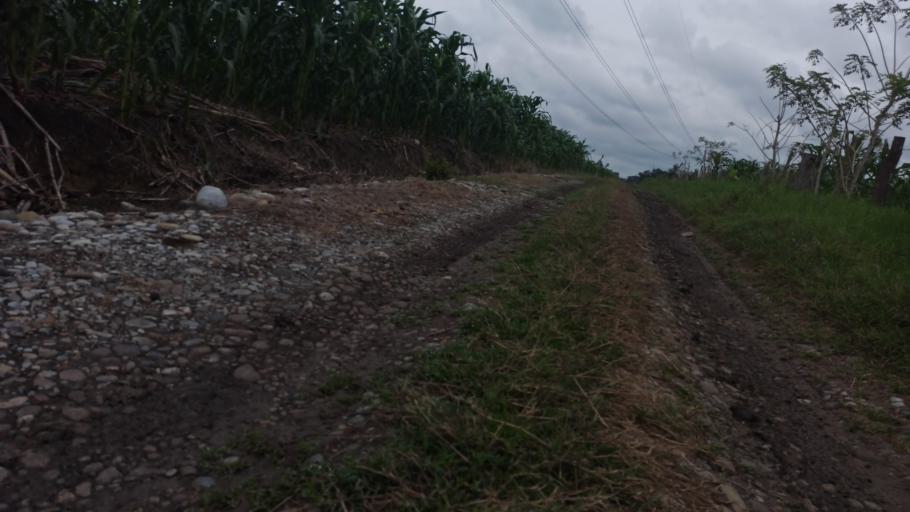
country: MX
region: Puebla
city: Espinal
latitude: 20.3028
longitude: -97.4106
